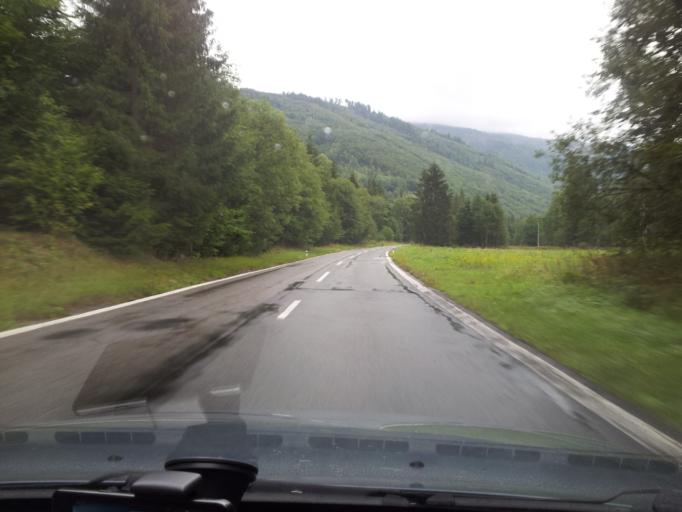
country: SK
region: Banskobystricky
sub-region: Okres Banska Bystrica
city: Brezno
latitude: 48.8731
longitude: 19.6535
